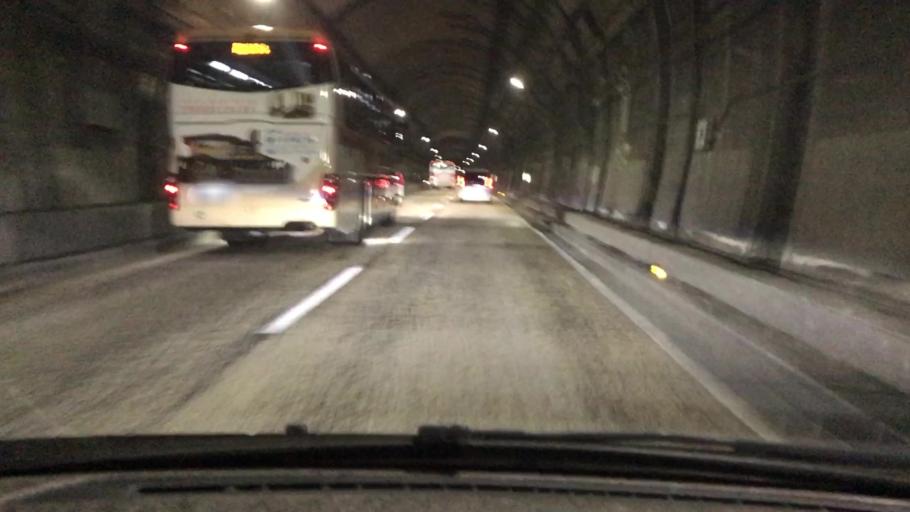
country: JP
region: Hyogo
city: Kobe
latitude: 34.7108
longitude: 135.1919
